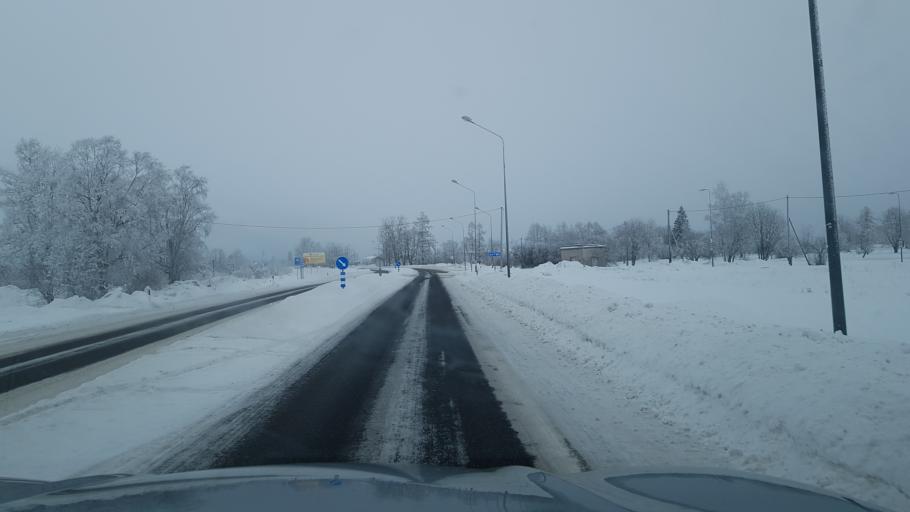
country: EE
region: Ida-Virumaa
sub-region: Johvi vald
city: Johvi
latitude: 59.3290
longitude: 27.4014
